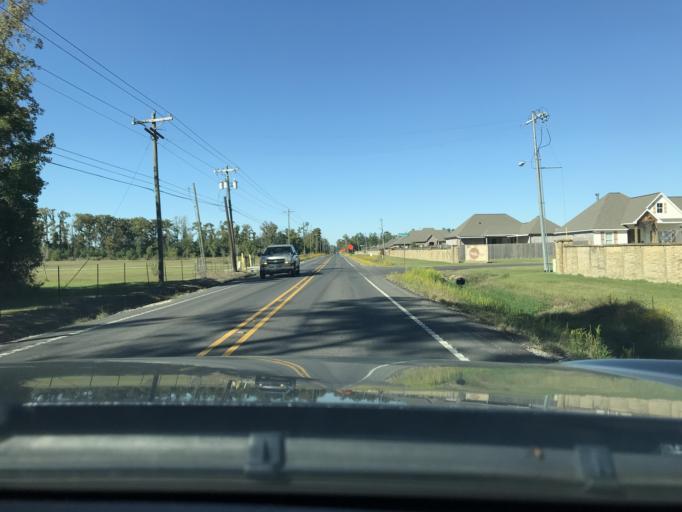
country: US
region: Louisiana
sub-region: Calcasieu Parish
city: Westlake
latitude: 30.3080
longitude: -93.2584
